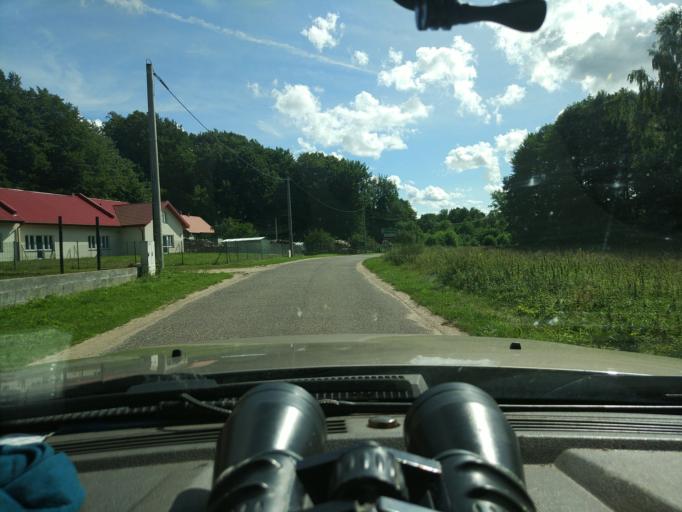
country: PL
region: Pomeranian Voivodeship
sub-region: Powiat wejherowski
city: Choczewo
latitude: 54.7586
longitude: 17.7925
